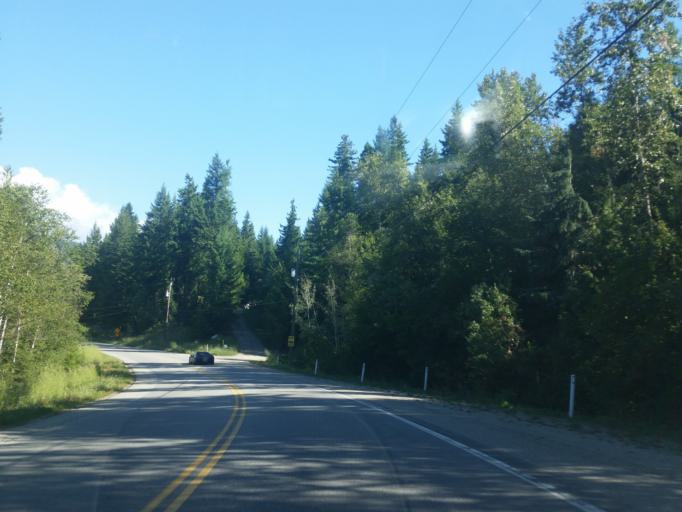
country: CA
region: British Columbia
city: Sicamous
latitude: 50.7032
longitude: -119.0362
